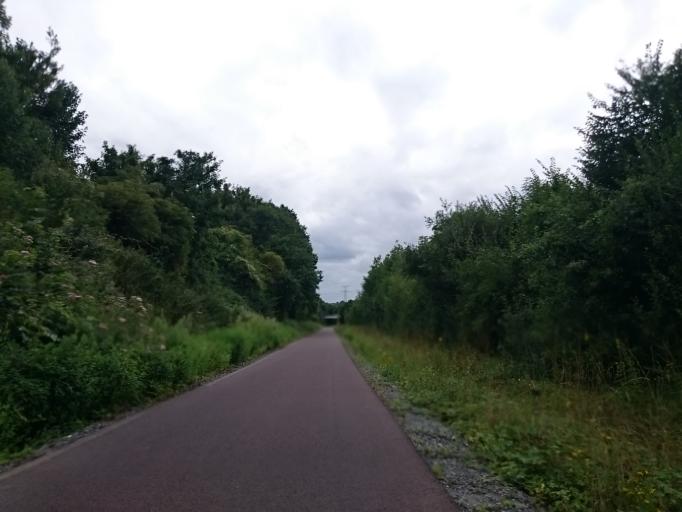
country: FR
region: Lower Normandy
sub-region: Departement du Calvados
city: Louvigny
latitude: 49.1343
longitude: -0.3989
